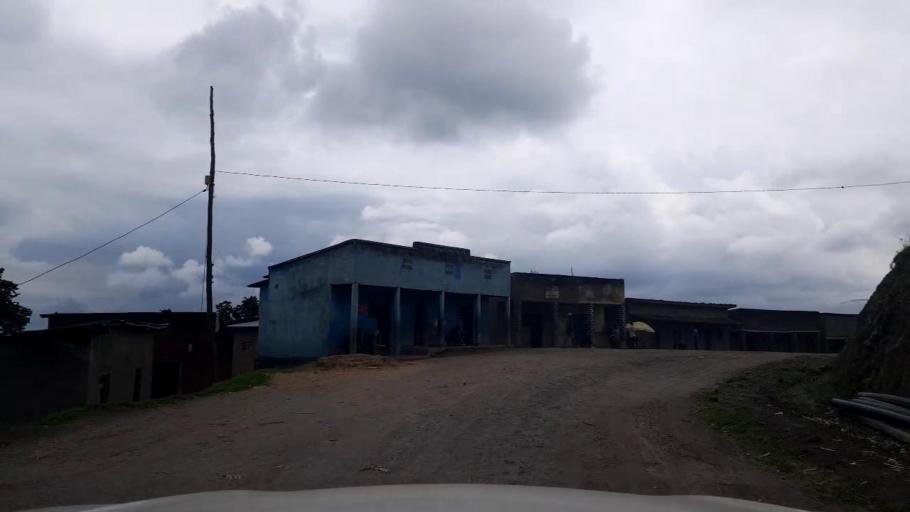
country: RW
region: Northern Province
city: Musanze
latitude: -1.5309
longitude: 29.5329
